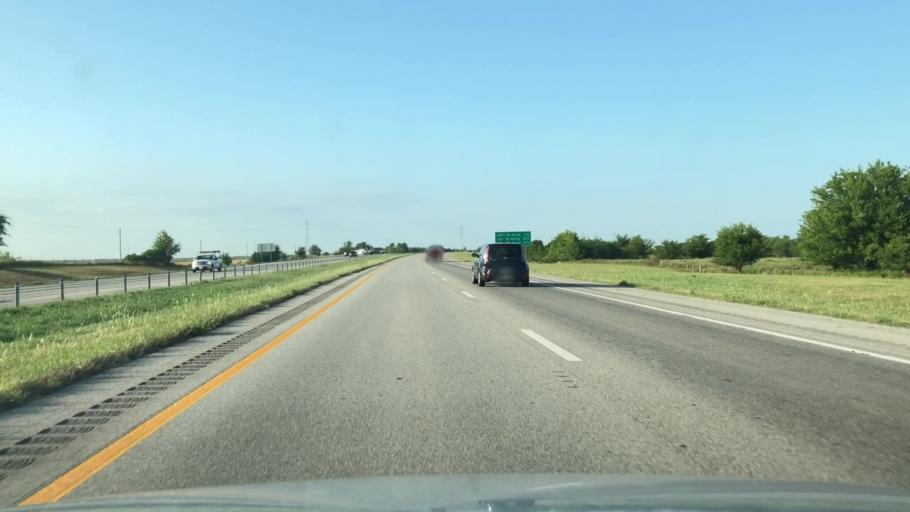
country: US
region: Oklahoma
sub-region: Osage County
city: Skiatook
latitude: 36.3556
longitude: -95.9208
